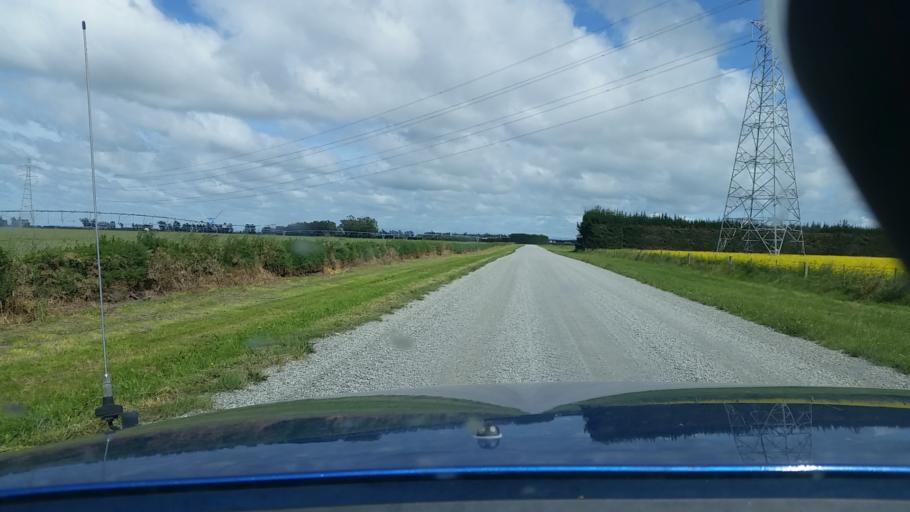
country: NZ
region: Canterbury
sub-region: Ashburton District
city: Rakaia
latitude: -43.8359
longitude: 171.9774
